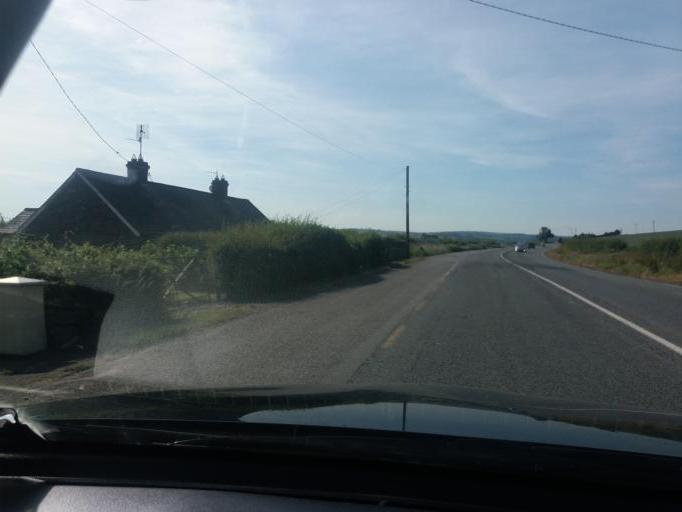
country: IE
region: Leinster
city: Lusk
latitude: 53.5286
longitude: -6.1902
